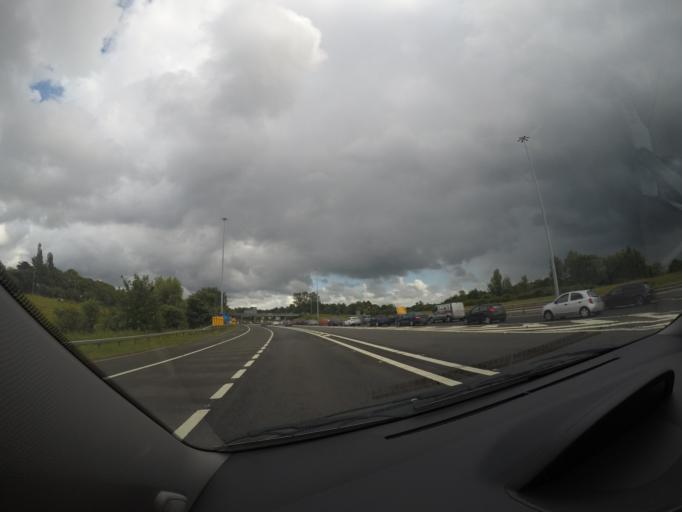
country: GB
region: Scotland
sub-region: South Lanarkshire
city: Uddingston
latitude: 55.8306
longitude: -4.0971
